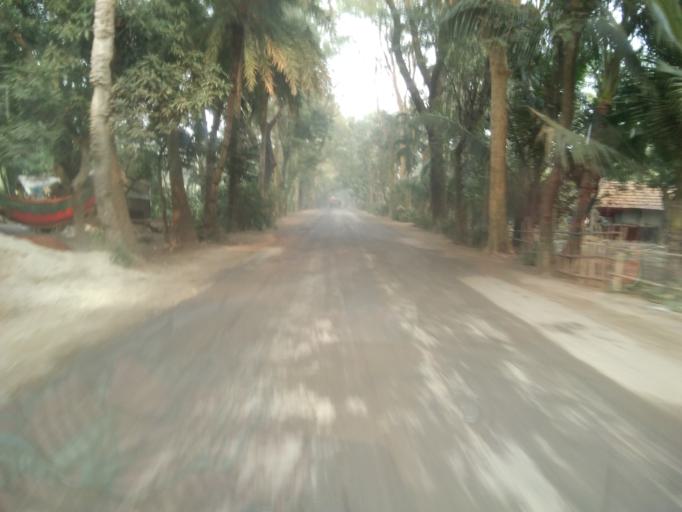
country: BD
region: Khulna
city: Satkhira
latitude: 22.6768
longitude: 89.0181
